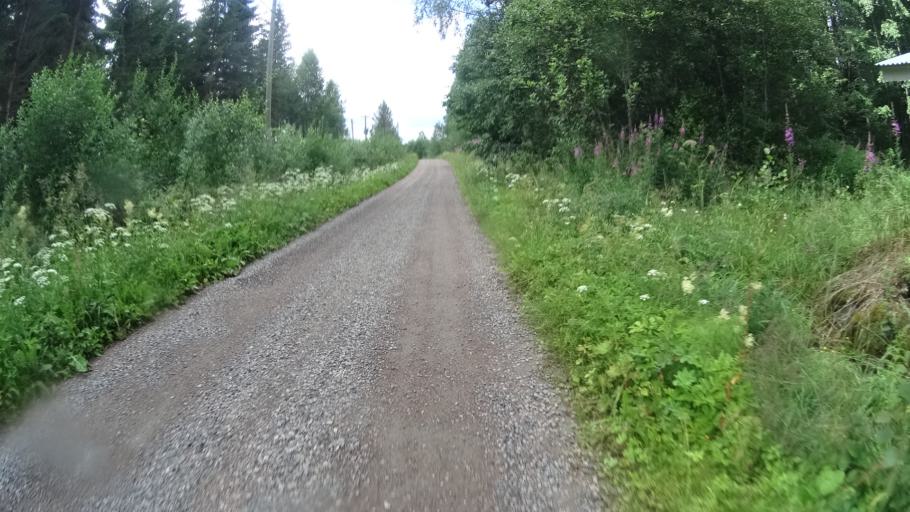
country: FI
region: Uusimaa
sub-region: Helsinki
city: Karkkila
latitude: 60.6064
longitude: 24.1895
